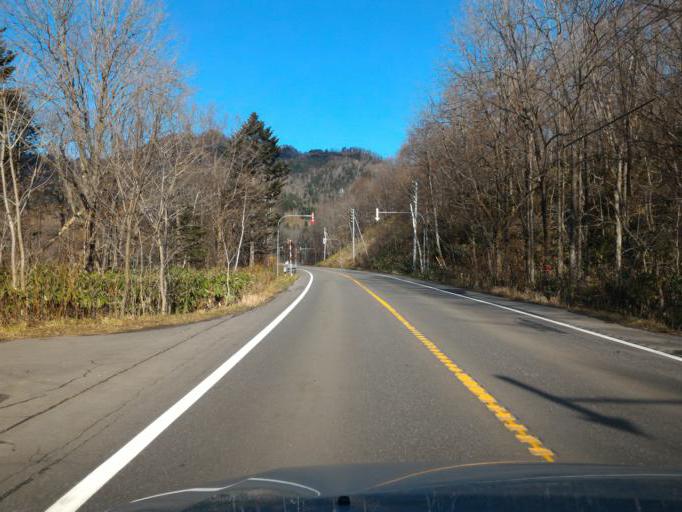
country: JP
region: Hokkaido
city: Ashibetsu
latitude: 43.3654
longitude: 142.1634
